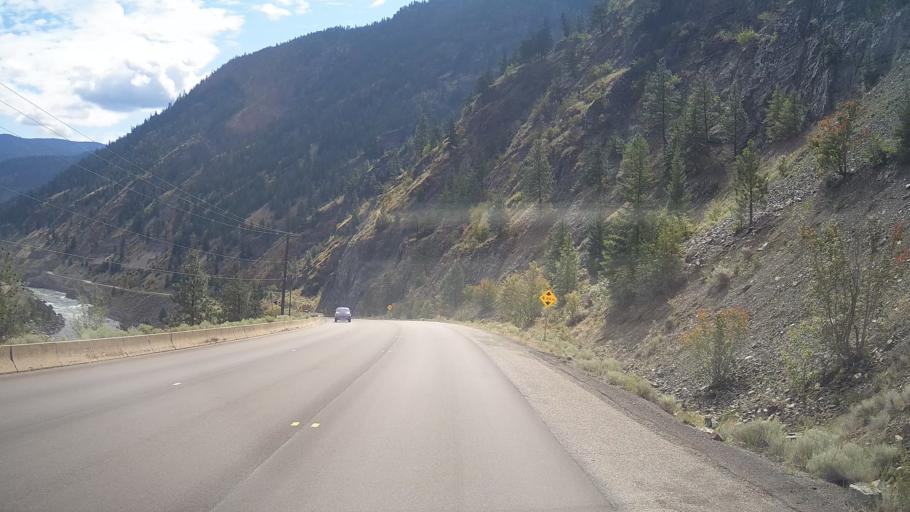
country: CA
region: British Columbia
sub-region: Thompson-Nicola Regional District
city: Ashcroft
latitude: 50.2560
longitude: -121.4540
